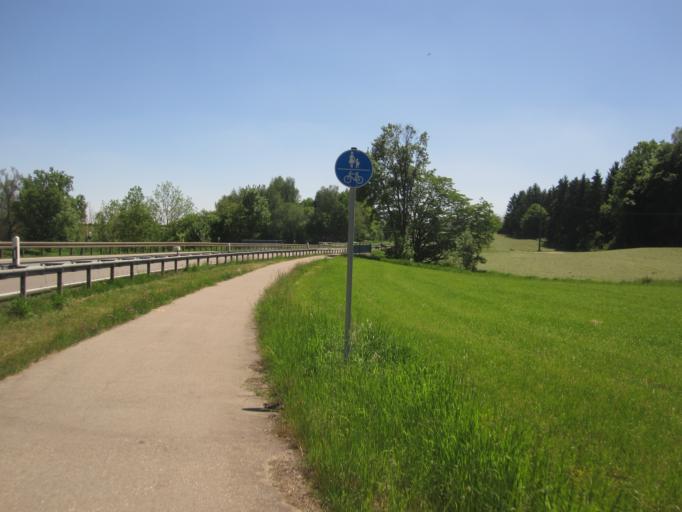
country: DE
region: Baden-Wuerttemberg
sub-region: Tuebingen Region
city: Nerenstetten
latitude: 48.5345
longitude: 10.0923
